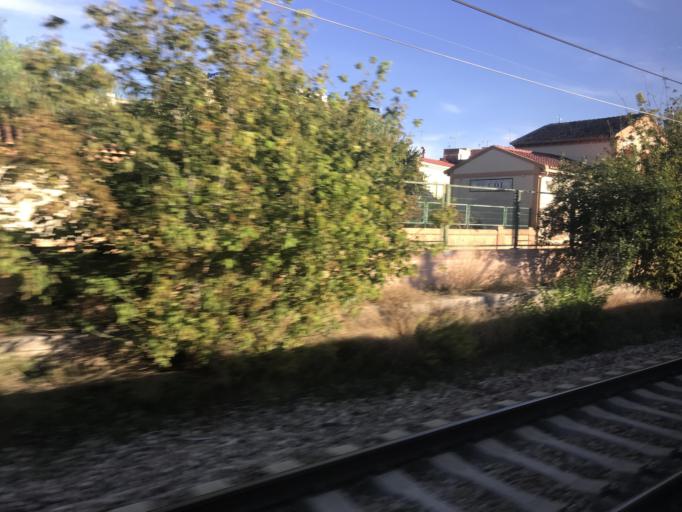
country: ES
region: Valencia
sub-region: Provincia de Valencia
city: Pucol
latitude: 39.6176
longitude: -0.3048
